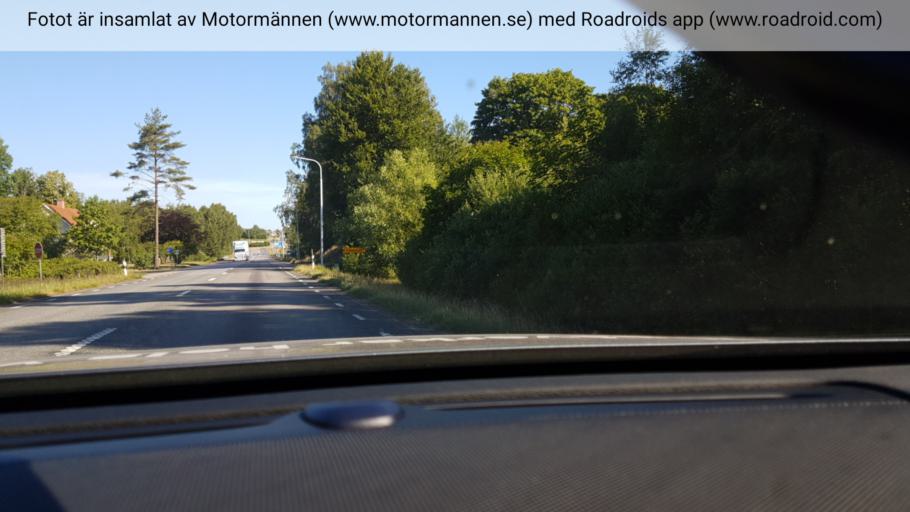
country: SE
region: Kronoberg
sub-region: Markaryds Kommun
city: Markaryd
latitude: 56.4419
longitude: 13.6054
